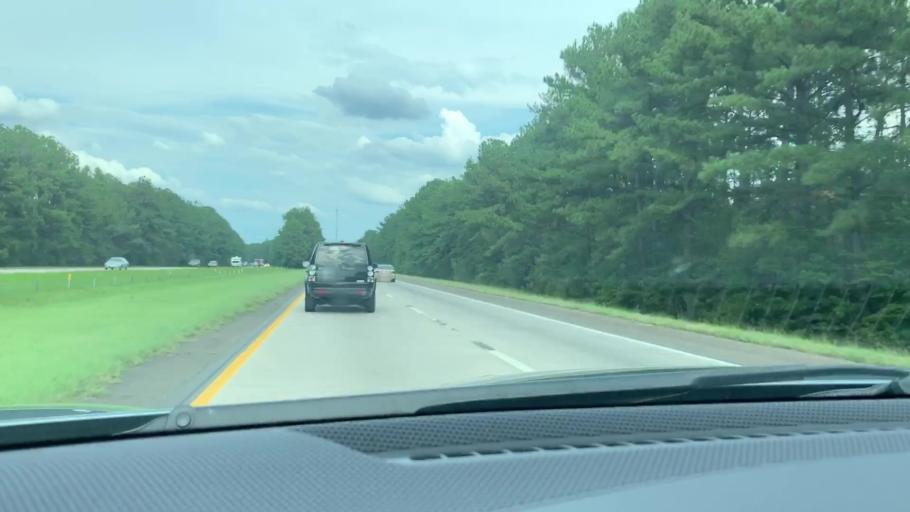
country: US
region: South Carolina
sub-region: Hampton County
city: Yemassee
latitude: 32.7858
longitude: -80.7841
